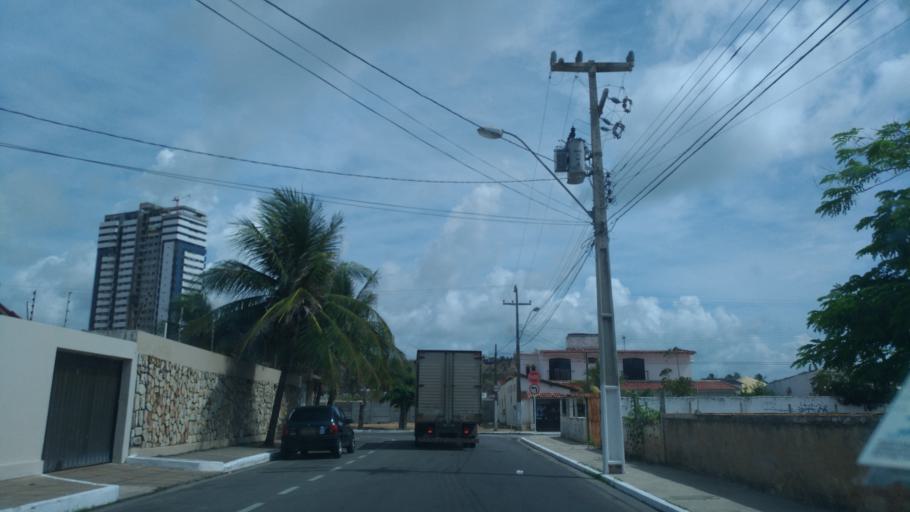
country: BR
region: Alagoas
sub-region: Maceio
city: Maceio
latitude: -9.6266
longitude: -35.6958
